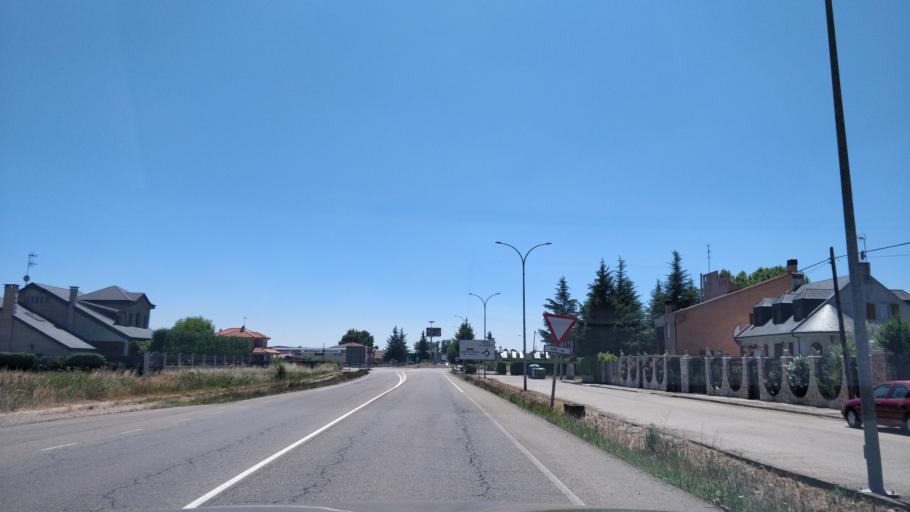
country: ES
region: Castille and Leon
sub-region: Provincia de Leon
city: La Baneza
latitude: 42.3142
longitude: -5.8926
